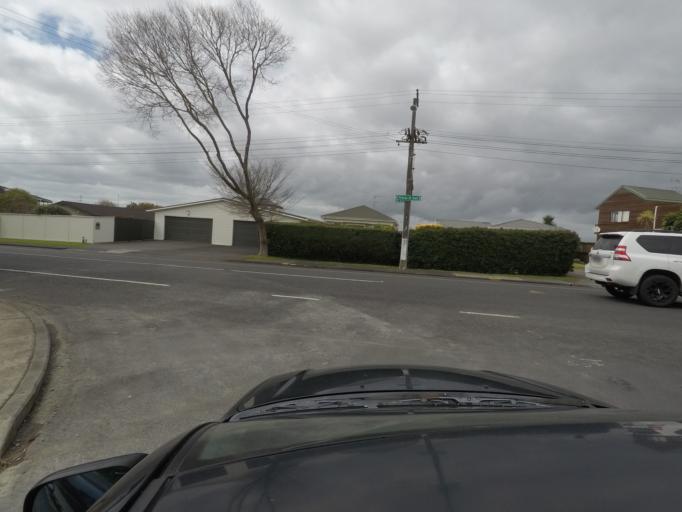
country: NZ
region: Auckland
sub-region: Auckland
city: Tamaki
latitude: -36.9367
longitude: 174.8589
